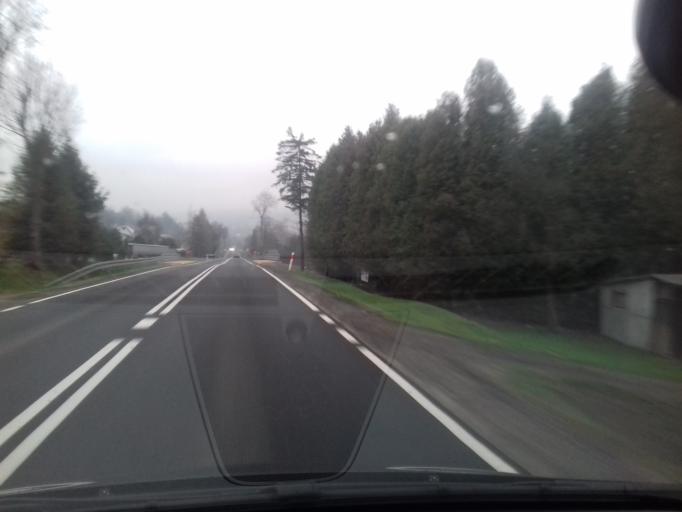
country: PL
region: Lesser Poland Voivodeship
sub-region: Powiat limanowski
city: Dobra
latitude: 49.7093
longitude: 20.2466
